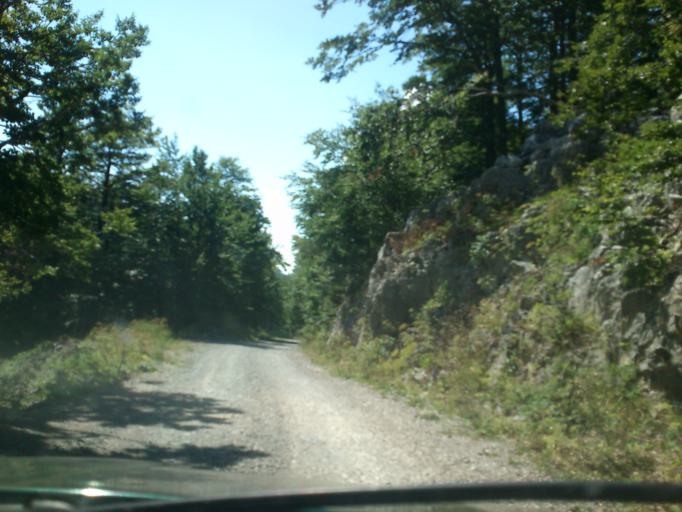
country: HR
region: Licko-Senjska
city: Senj
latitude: 44.8208
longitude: 14.9871
